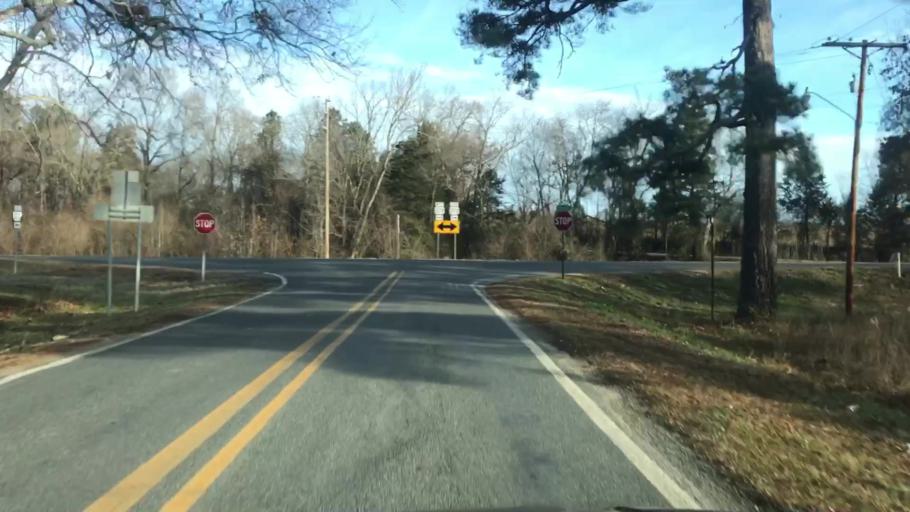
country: US
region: Arkansas
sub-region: Garland County
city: Rockwell
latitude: 34.5104
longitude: -93.2760
